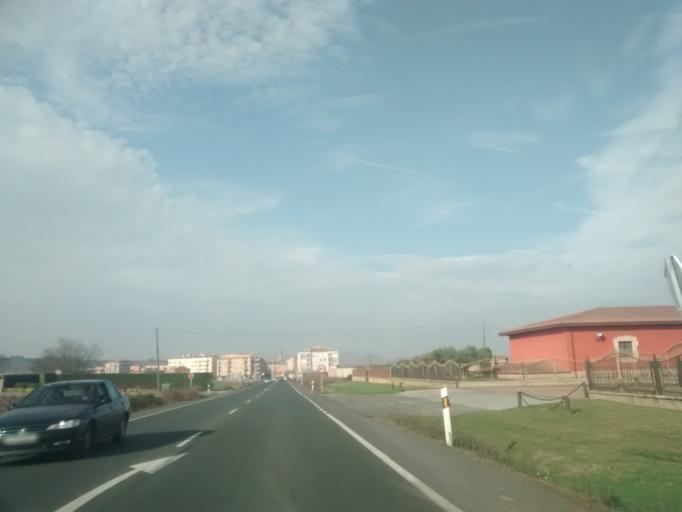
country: ES
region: La Rioja
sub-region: Provincia de La Rioja
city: Fuenmayor
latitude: 42.4600
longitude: -2.5566
